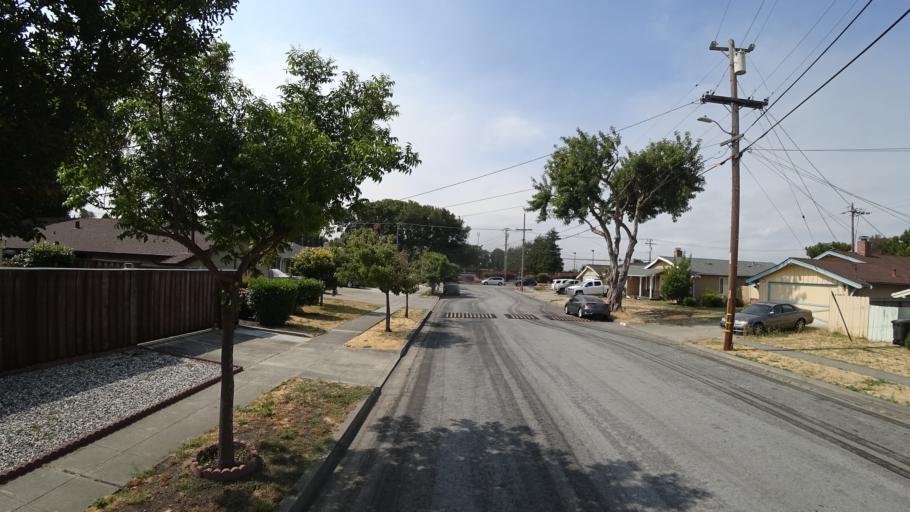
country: US
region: California
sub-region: Alameda County
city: Hayward
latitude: 37.6323
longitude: -122.1008
